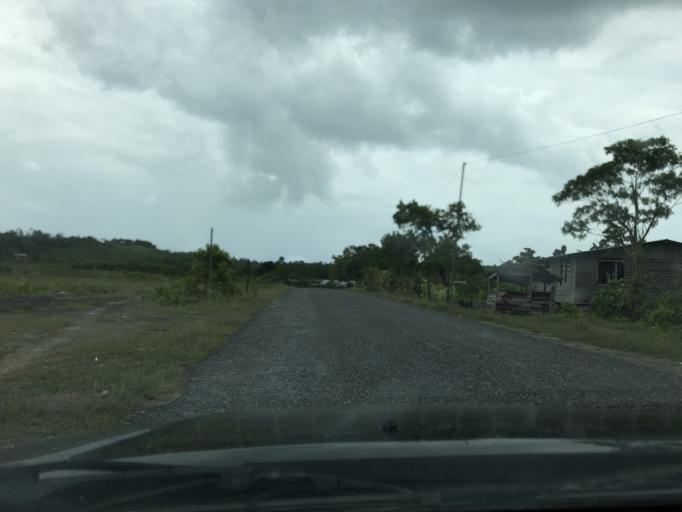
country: SB
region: Western Province
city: Gizo
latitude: -8.3268
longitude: 157.2716
